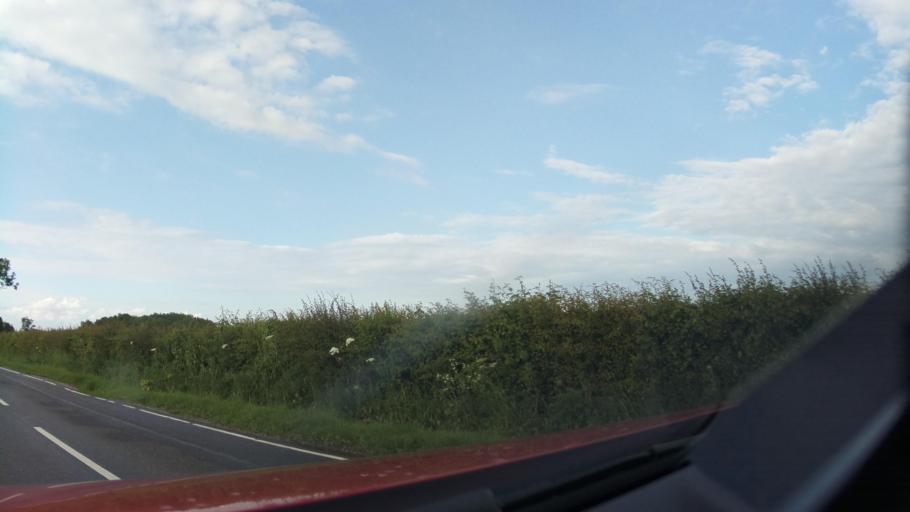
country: GB
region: England
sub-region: Lincolnshire
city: Great Gonerby
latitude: 53.0144
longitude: -0.6616
